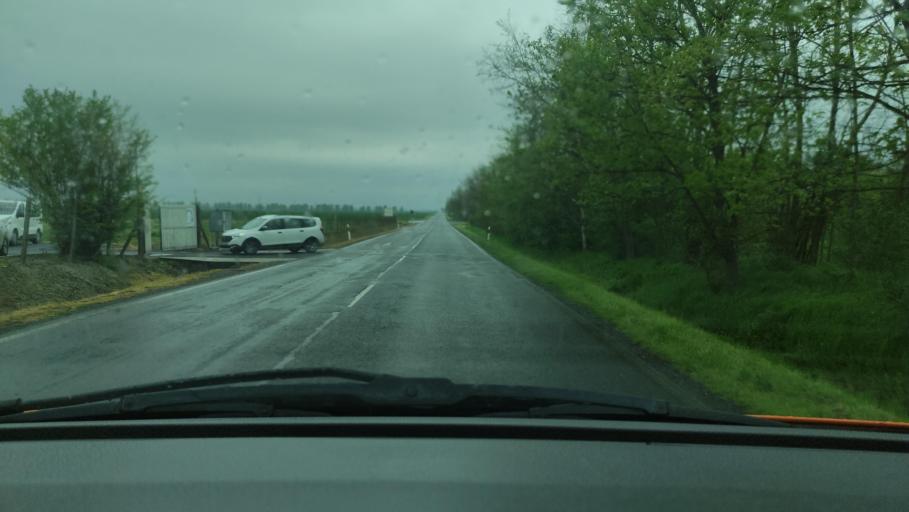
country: HU
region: Baranya
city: Mohacs
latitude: 45.9284
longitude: 18.6598
